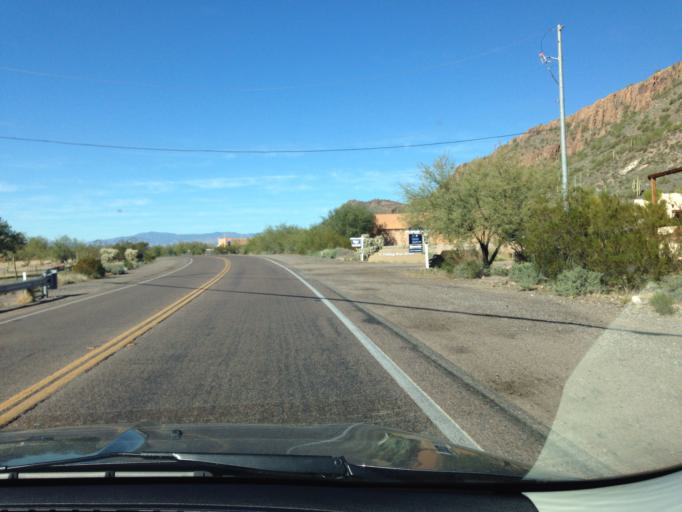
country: US
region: Arizona
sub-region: Maricopa County
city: Anthem
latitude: 33.8649
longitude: -112.0587
